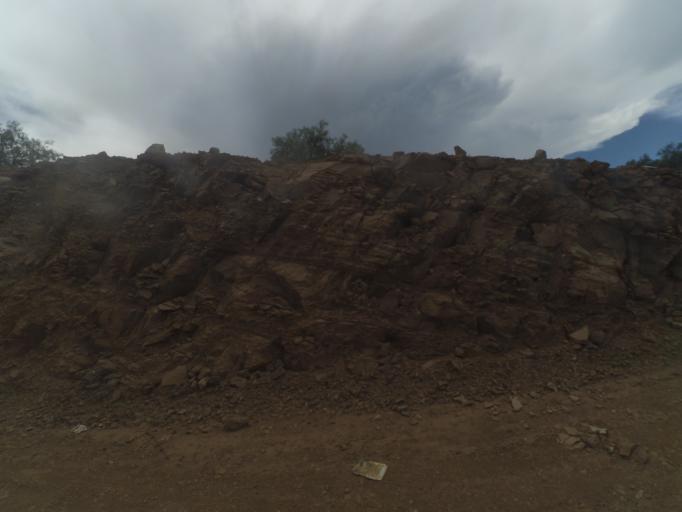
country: BO
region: Chuquisaca
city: Padilla
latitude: -19.3470
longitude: -64.2915
